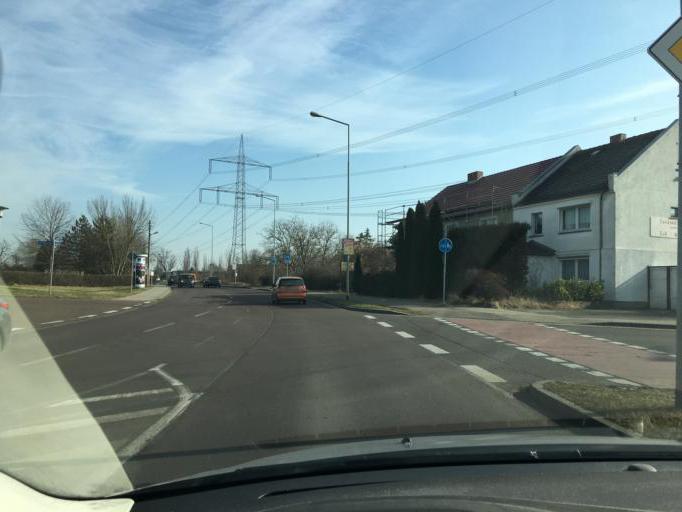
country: DE
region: Saxony-Anhalt
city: Schkopau
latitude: 51.4363
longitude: 11.9763
